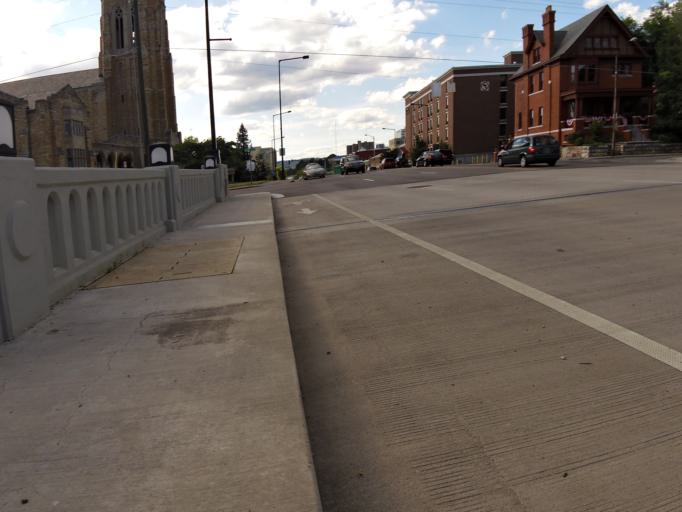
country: US
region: Tennessee
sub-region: Knox County
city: Knoxville
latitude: 35.9589
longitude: -83.9199
